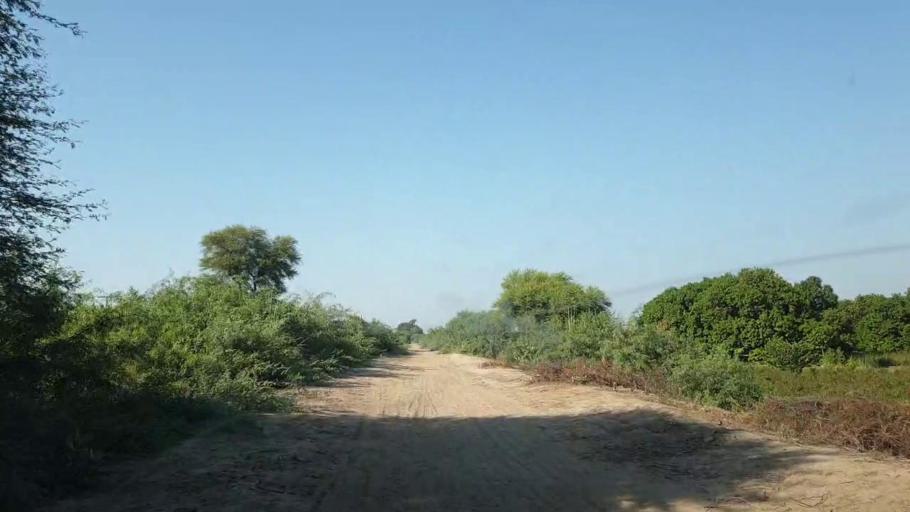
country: PK
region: Sindh
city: Tando Jam
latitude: 25.3676
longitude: 68.5693
